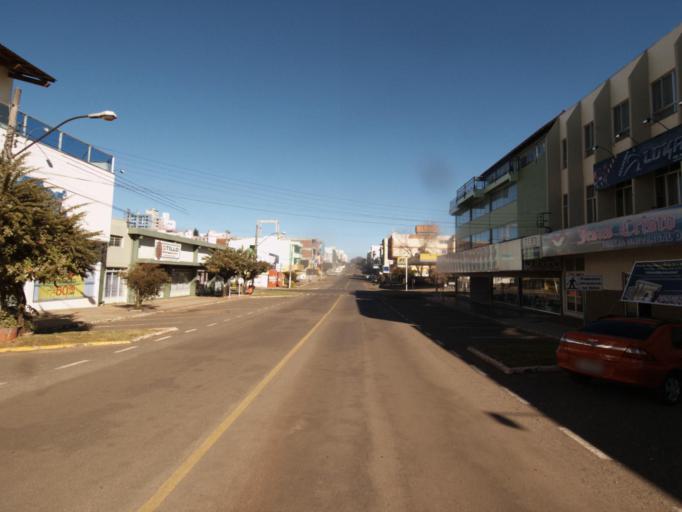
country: AR
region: Misiones
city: Bernardo de Irigoyen
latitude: -26.7265
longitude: -53.5204
